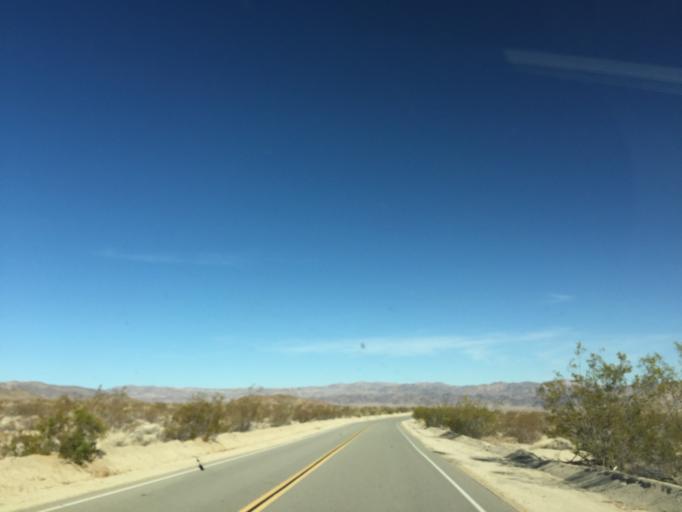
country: US
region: California
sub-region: San Bernardino County
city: Twentynine Palms
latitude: 33.8749
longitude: -115.8084
